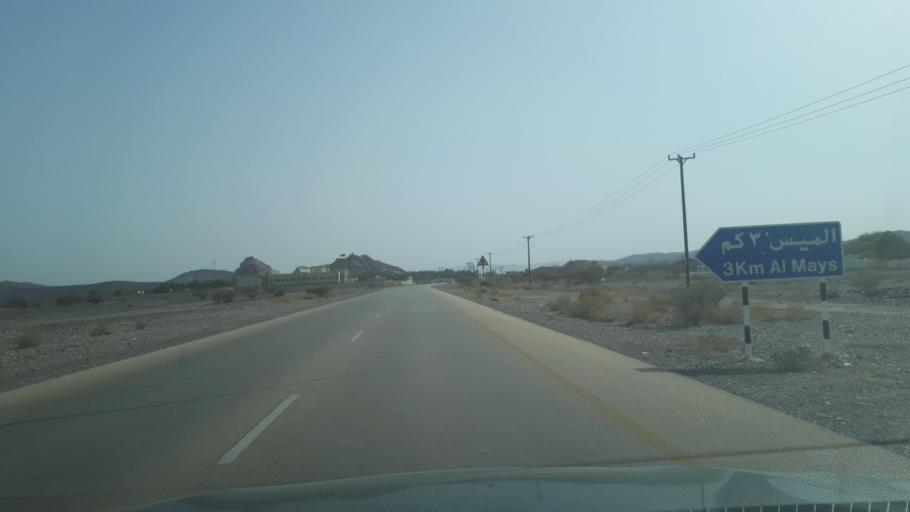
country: OM
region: Az Zahirah
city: `Ibri
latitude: 23.1497
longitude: 56.9066
